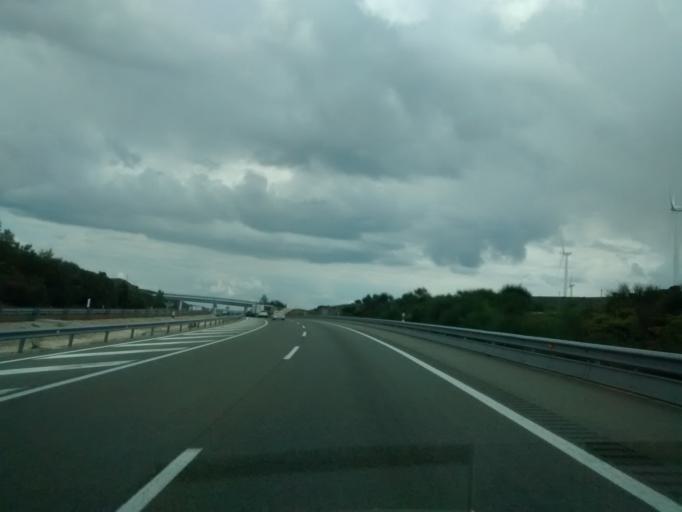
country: ES
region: Castille-La Mancha
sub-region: Provincia de Guadalajara
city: Alcolea del Pinar
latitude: 41.0968
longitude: -2.4507
